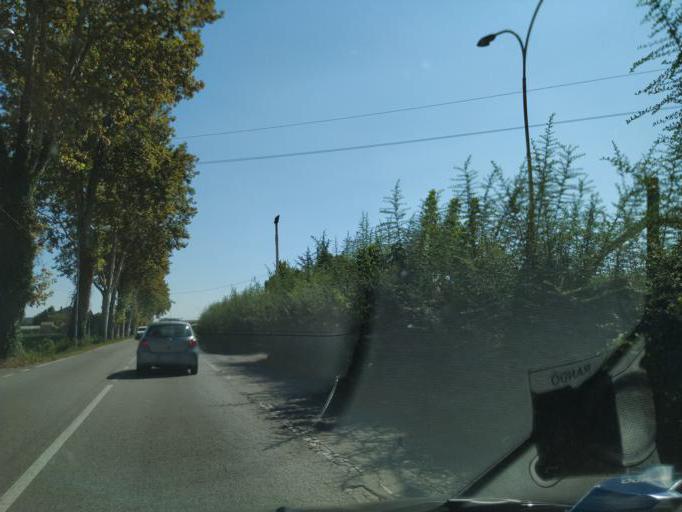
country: IT
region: Emilia-Romagna
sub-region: Provincia di Ferrara
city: La Saletta-Tamara
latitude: 44.8808
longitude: 11.7528
